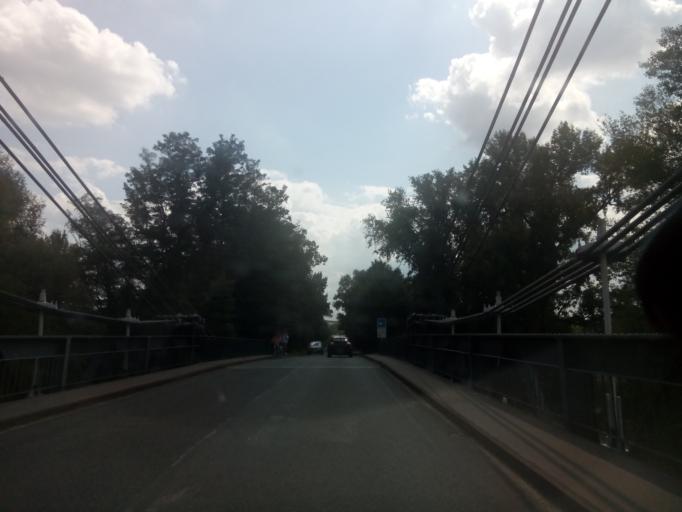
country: FR
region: Centre
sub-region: Departement d'Indre-et-Loire
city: Langeais
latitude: 47.3183
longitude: 0.4054
